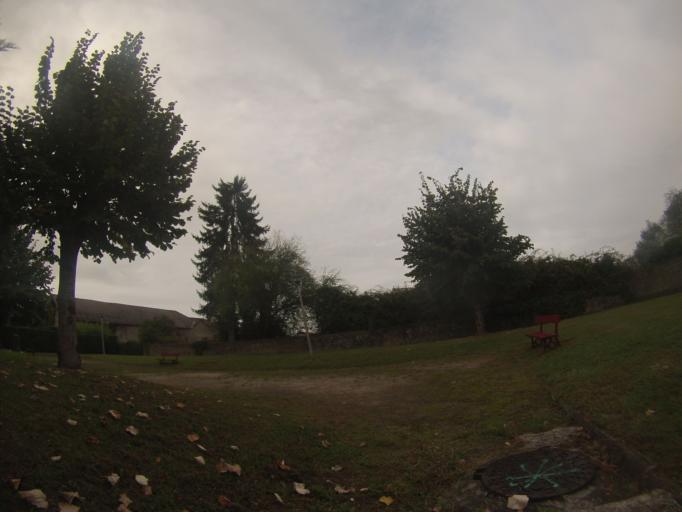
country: FR
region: Aquitaine
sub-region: Departement des Pyrenees-Atlantiques
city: Gelos
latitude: 43.2751
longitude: -0.3591
